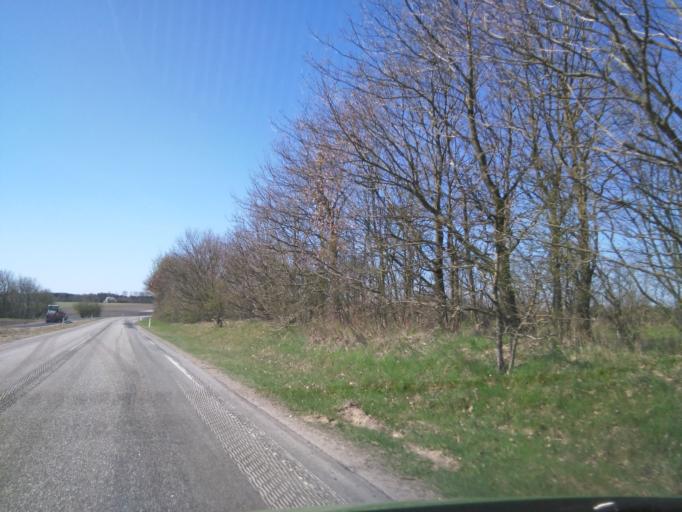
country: DK
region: South Denmark
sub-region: Billund Kommune
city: Billund
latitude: 55.7069
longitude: 9.0245
